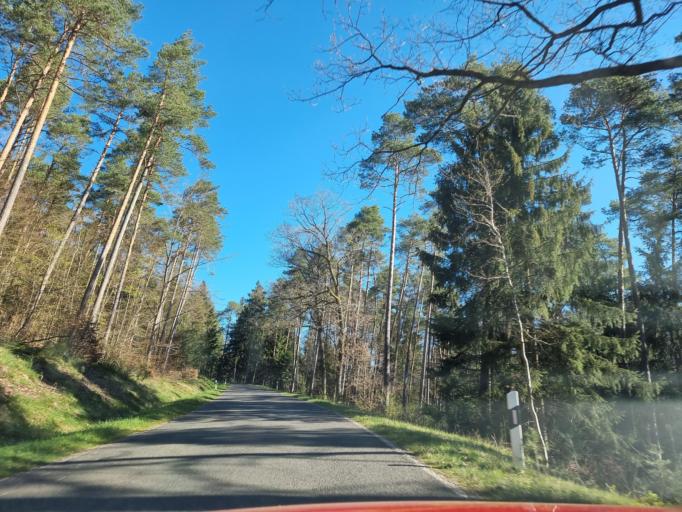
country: DE
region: Rheinland-Pfalz
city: Heckenmunster
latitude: 49.8881
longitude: 6.7731
